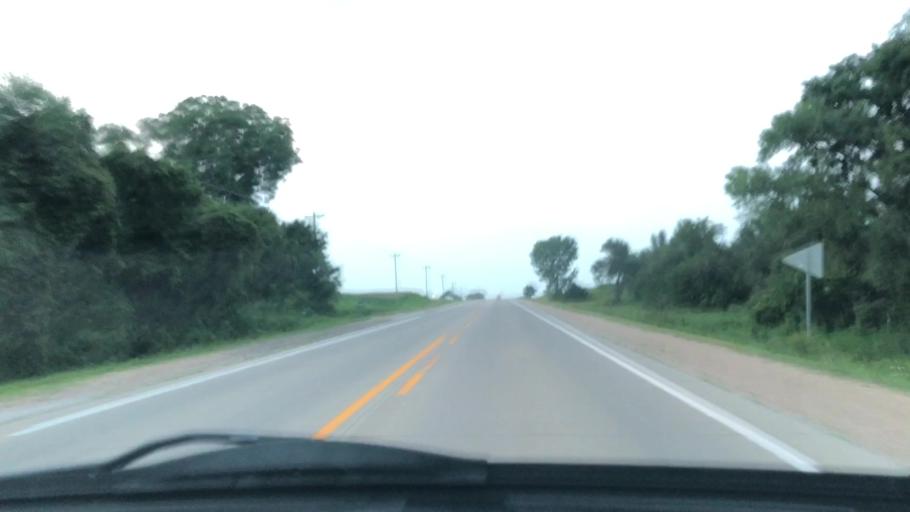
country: US
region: Iowa
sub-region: Linn County
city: Ely
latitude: 41.8506
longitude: -91.6754
